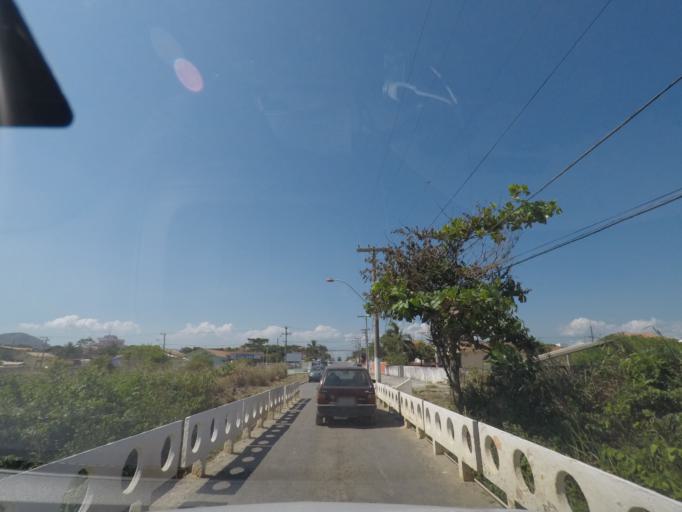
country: BR
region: Rio de Janeiro
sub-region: Marica
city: Marica
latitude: -22.9717
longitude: -42.9271
